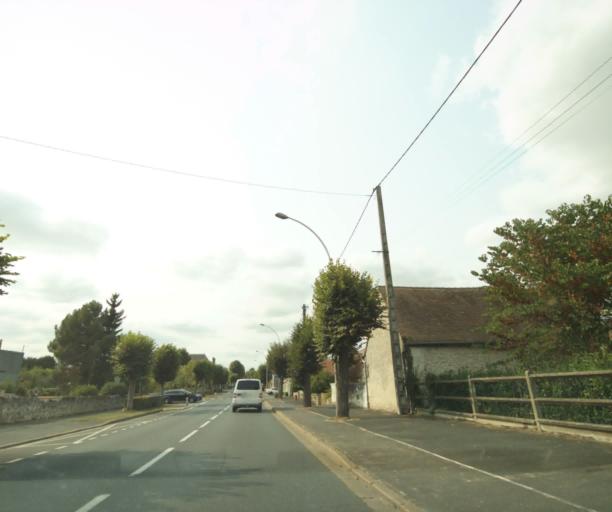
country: FR
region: Centre
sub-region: Departement de l'Indre
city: Chatillon-sur-Indre
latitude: 46.9928
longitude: 1.1653
